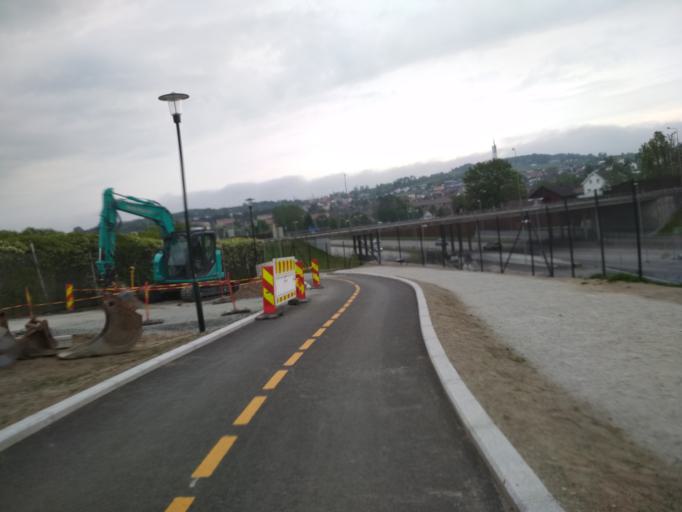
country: NO
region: Rogaland
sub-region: Stavanger
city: Stavanger
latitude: 58.9538
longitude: 5.7226
